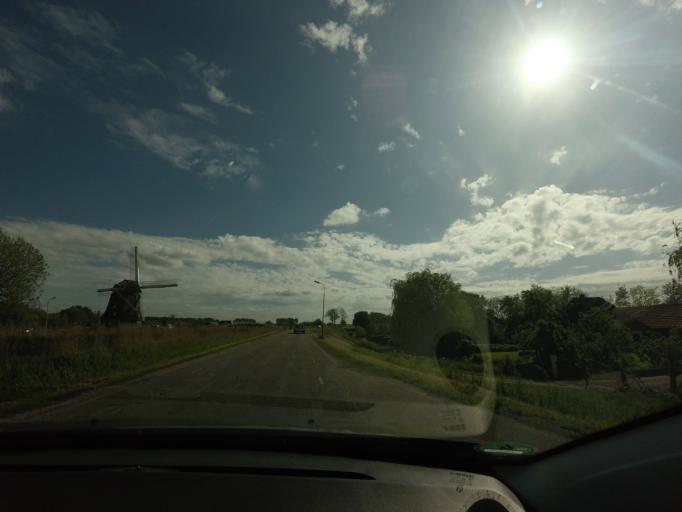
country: NL
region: North Holland
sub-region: Gemeente Heerhugowaard
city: Heerhugowaard
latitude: 52.6615
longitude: 4.8670
